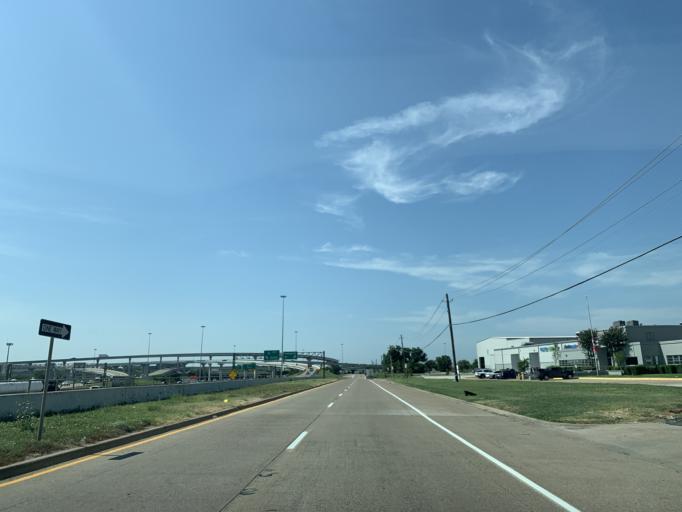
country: US
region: Texas
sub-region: Tarrant County
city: Edgecliff Village
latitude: 32.6736
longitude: -97.3209
